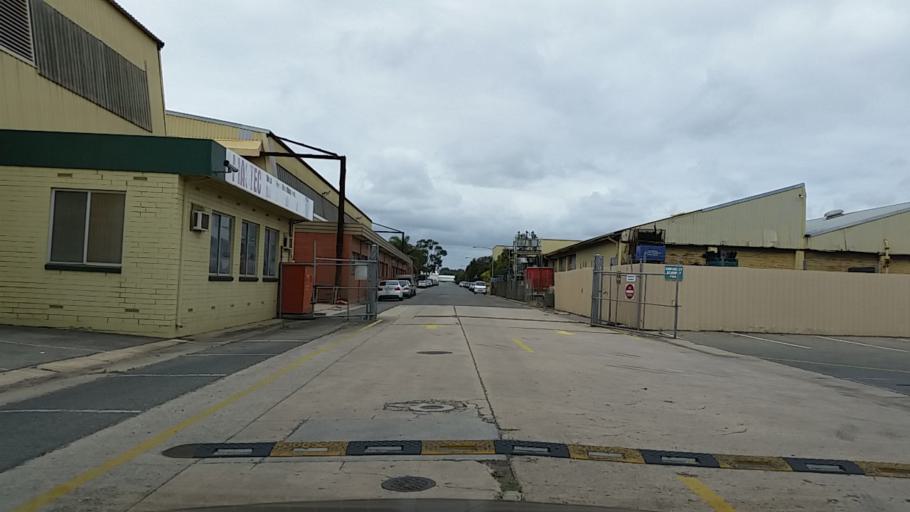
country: AU
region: South Australia
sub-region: Port Adelaide Enfield
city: Alberton
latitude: -34.8491
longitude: 138.5417
